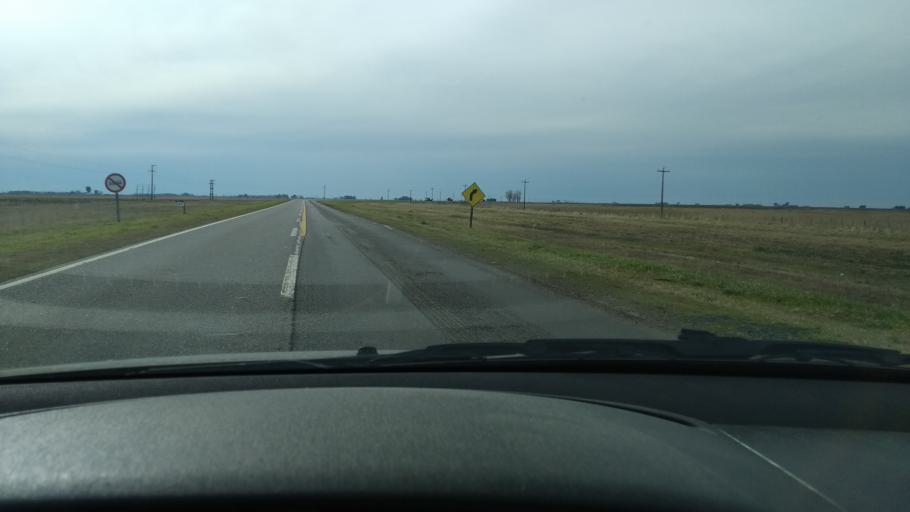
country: AR
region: Buenos Aires
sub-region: Partido de Azul
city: Azul
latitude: -36.7113
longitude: -59.7606
